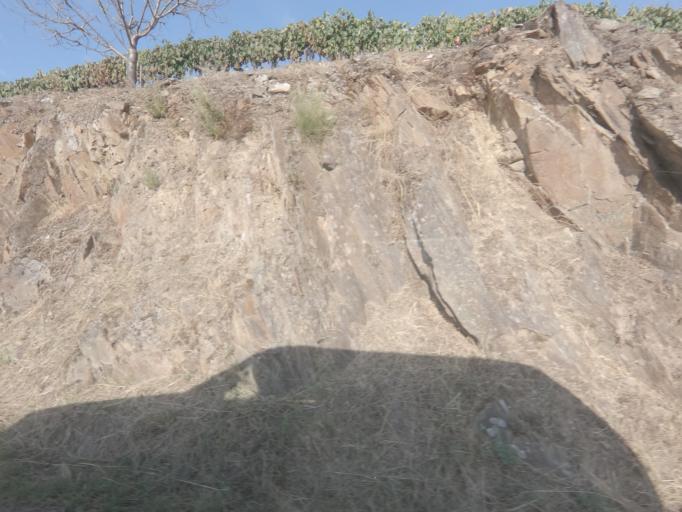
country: PT
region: Vila Real
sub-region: Sabrosa
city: Sabrosa
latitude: 41.2302
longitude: -7.5236
